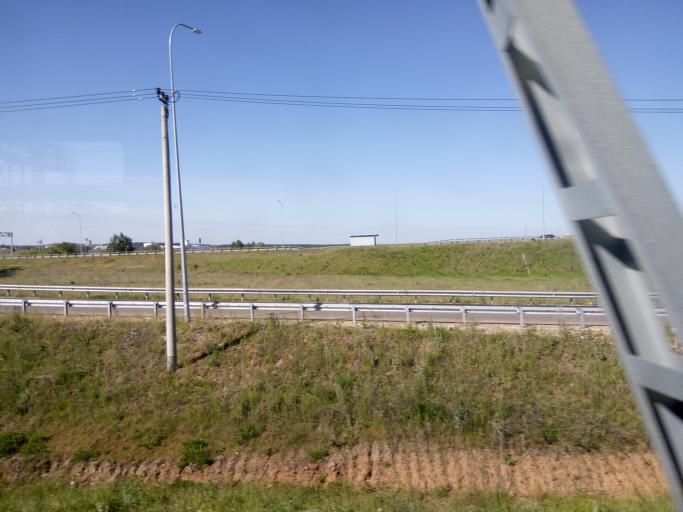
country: RU
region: Tatarstan
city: Stolbishchi
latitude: 55.6656
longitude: 49.2187
